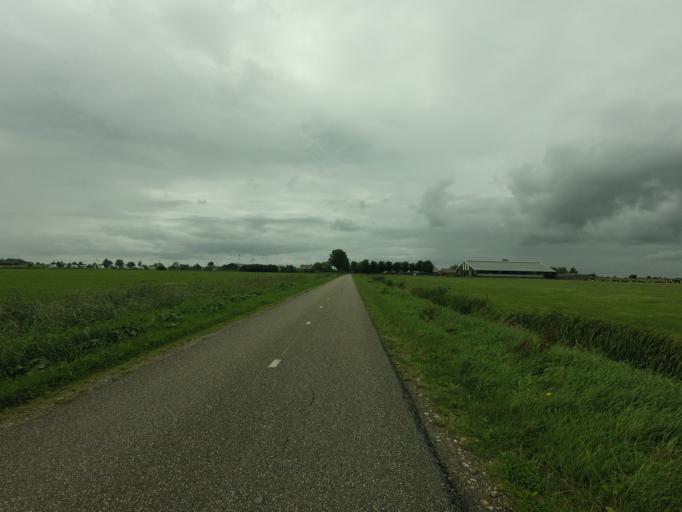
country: NL
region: Friesland
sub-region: Sudwest Fryslan
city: Workum
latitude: 52.9764
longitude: 5.5017
